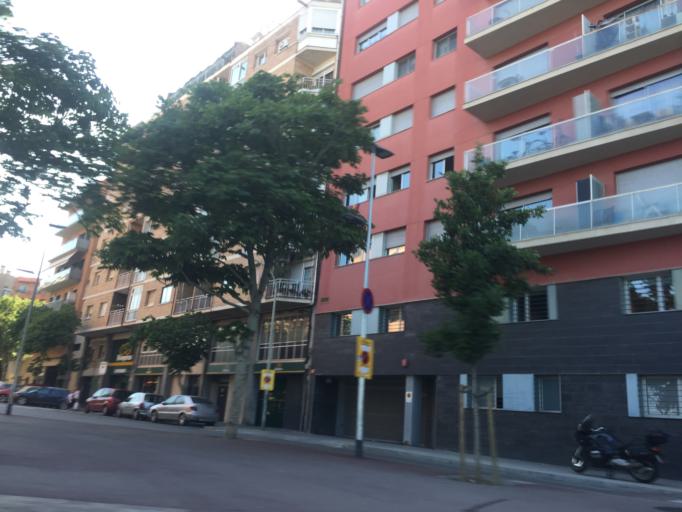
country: ES
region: Catalonia
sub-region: Provincia de Barcelona
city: Sant Marti
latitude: 41.4223
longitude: 2.1911
